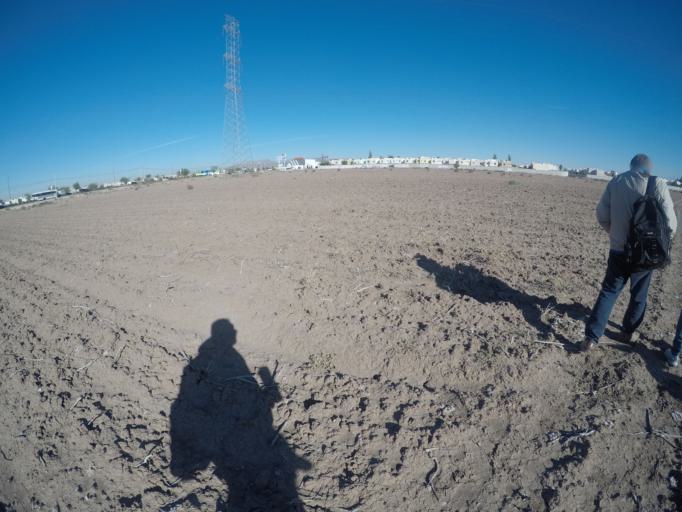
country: US
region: Texas
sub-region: El Paso County
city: Socorro
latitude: 31.6975
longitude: -106.3807
